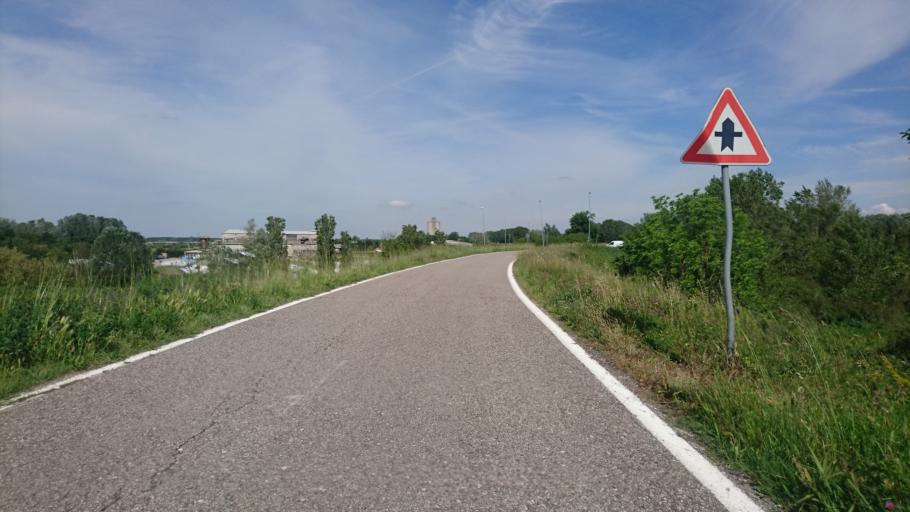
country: IT
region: Lombardy
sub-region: Provincia di Mantova
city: Revere
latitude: 45.0432
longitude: 11.1496
